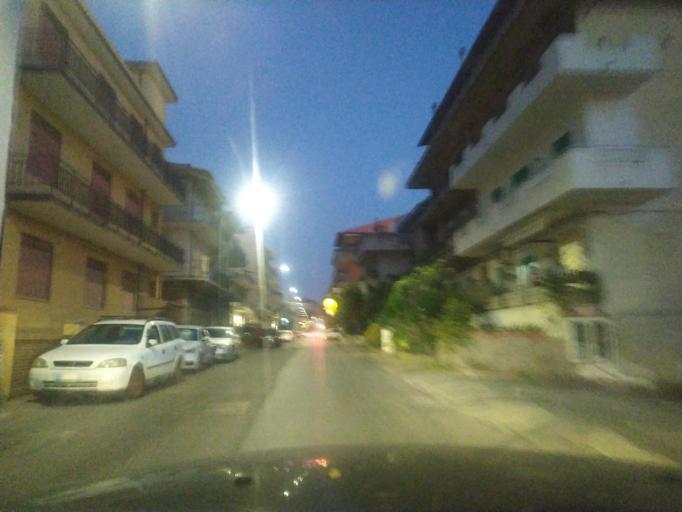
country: IT
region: Sicily
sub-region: Messina
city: Terme
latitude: 38.1399
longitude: 15.1612
